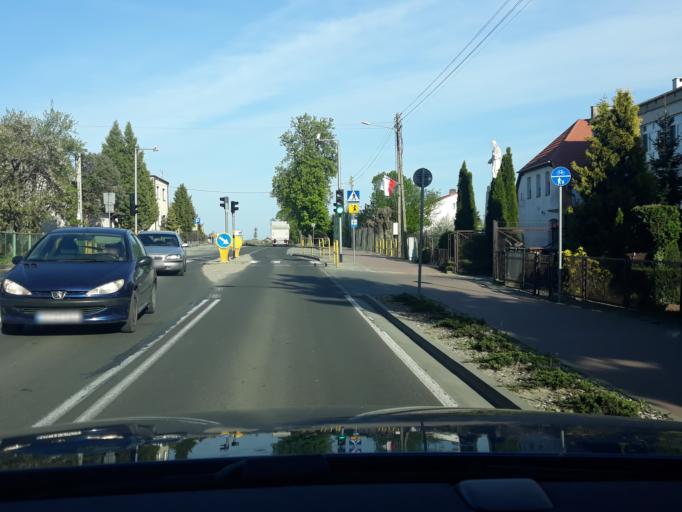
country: PL
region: Pomeranian Voivodeship
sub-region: Powiat czluchowski
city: Przechlewo
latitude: 53.8225
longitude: 17.3802
